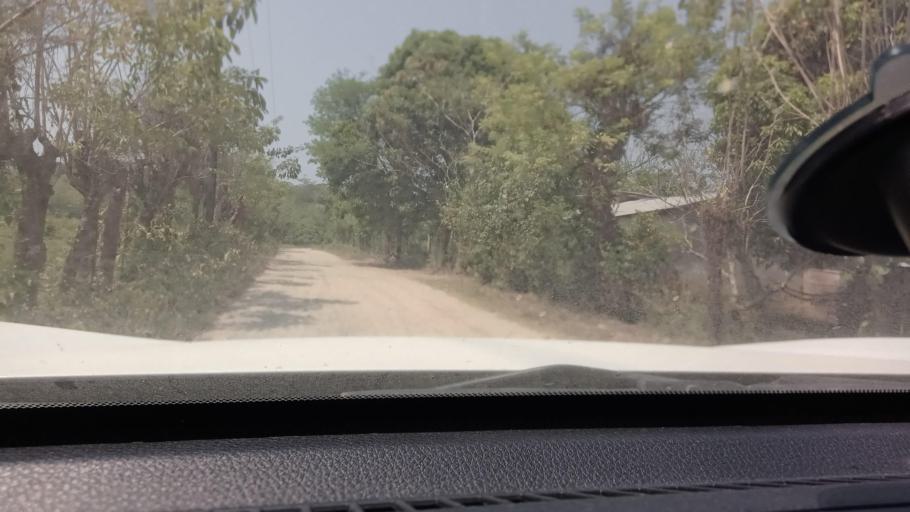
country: MX
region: Tabasco
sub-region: Huimanguillo
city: Francisco Rueda
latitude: 17.5079
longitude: -93.8990
